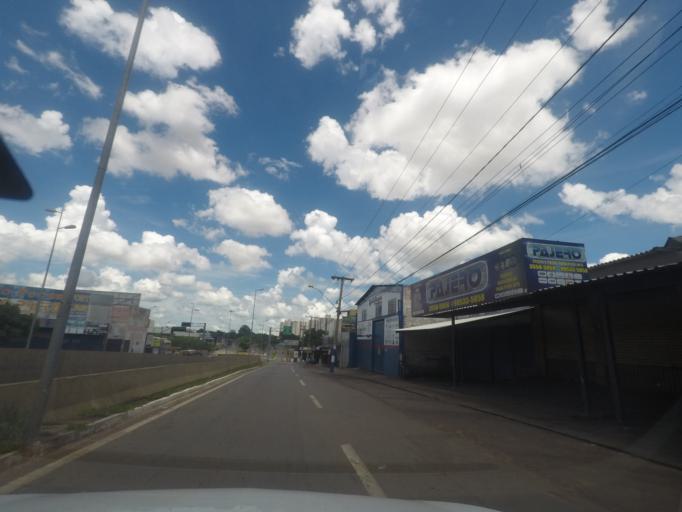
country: BR
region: Goias
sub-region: Goiania
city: Goiania
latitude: -16.6923
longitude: -49.3183
